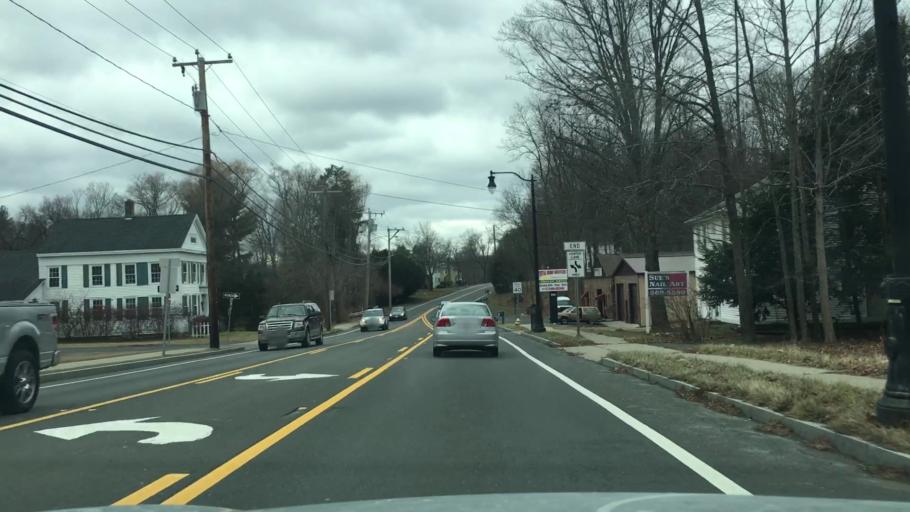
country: US
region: Massachusetts
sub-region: Hampden County
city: Southwick
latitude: 42.0533
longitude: -72.7720
